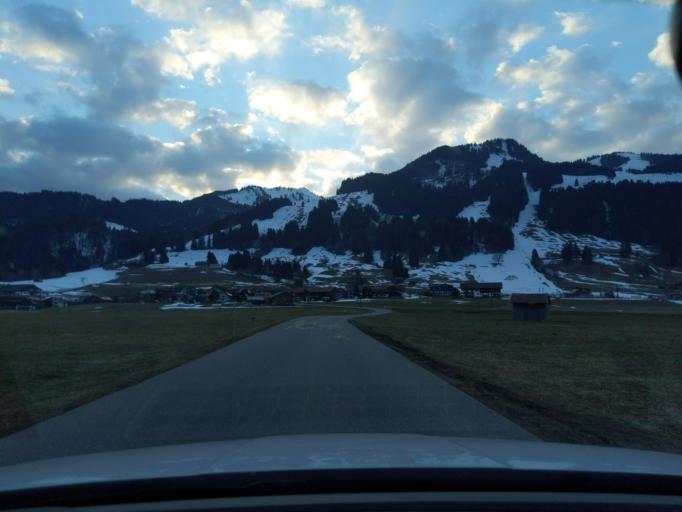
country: DE
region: Bavaria
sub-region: Swabia
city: Obermaiselstein
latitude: 47.4557
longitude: 10.2384
